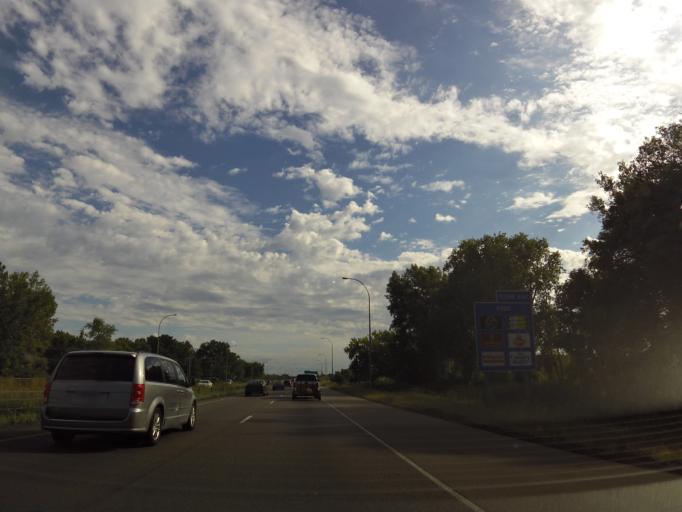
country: US
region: Minnesota
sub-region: Hennepin County
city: New Hope
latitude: 45.0651
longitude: -93.4010
